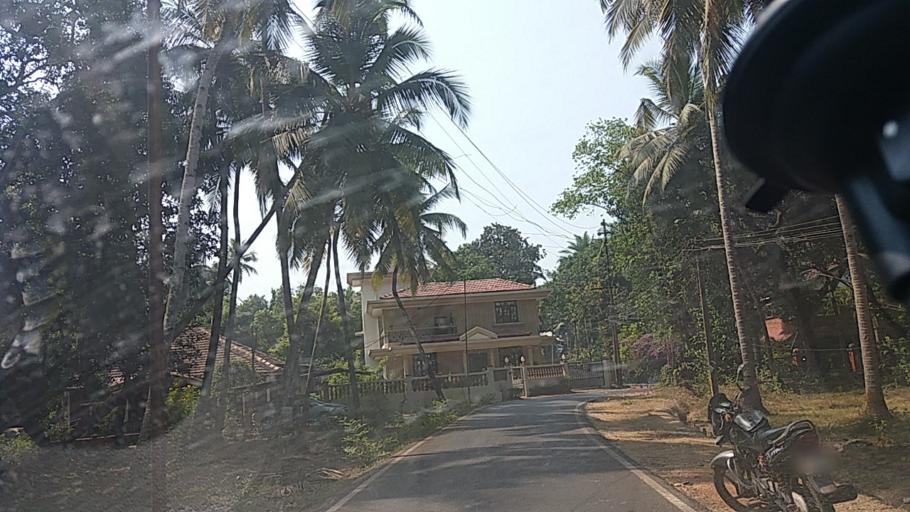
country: IN
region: Goa
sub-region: South Goa
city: Sancoale
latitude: 15.3365
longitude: 73.8980
